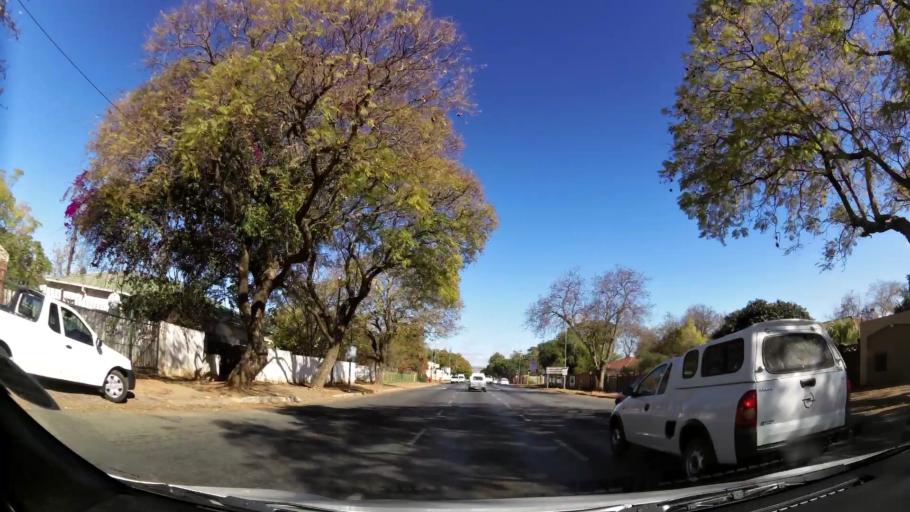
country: ZA
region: Limpopo
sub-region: Capricorn District Municipality
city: Polokwane
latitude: -23.9086
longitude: 29.4675
